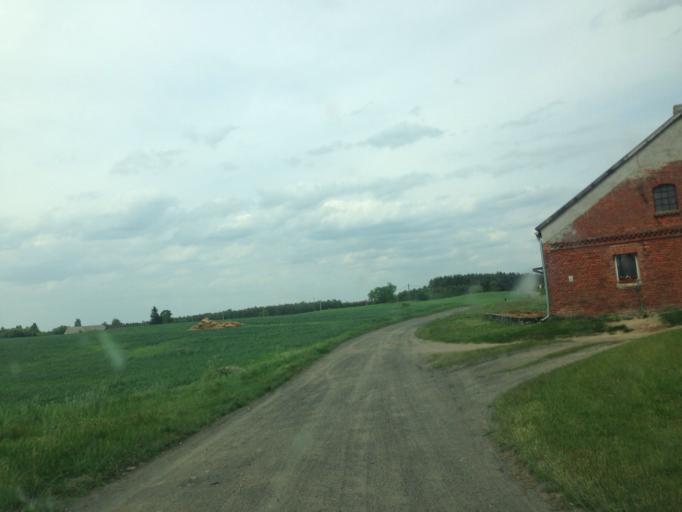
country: PL
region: Kujawsko-Pomorskie
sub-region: Powiat brodnicki
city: Brodnica
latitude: 53.3092
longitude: 19.3583
